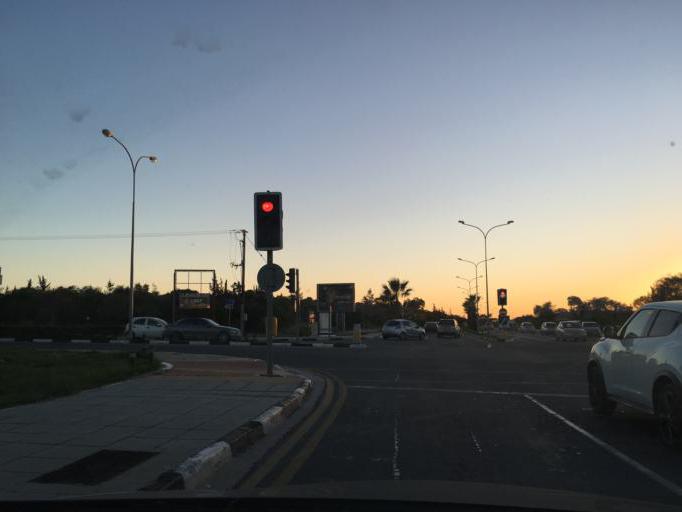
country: CY
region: Larnaka
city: Larnaca
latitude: 34.8914
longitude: 33.6312
